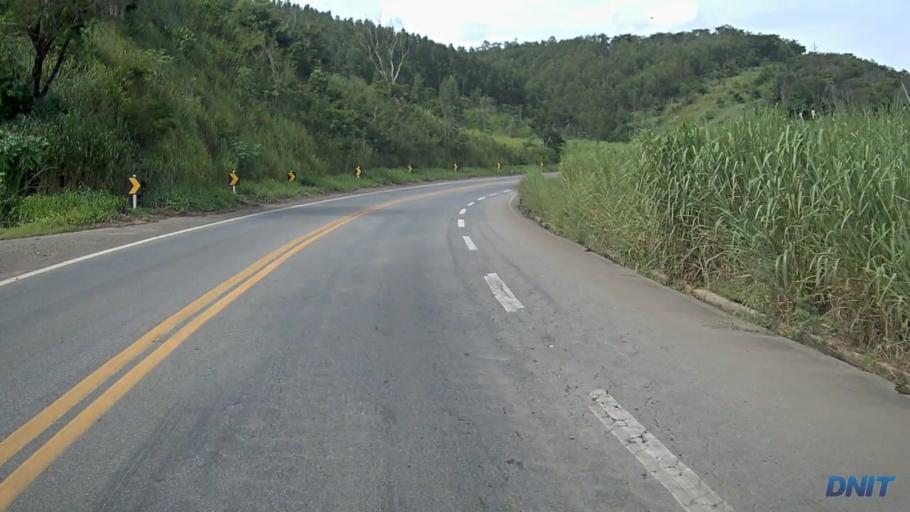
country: BR
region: Minas Gerais
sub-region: Ipaba
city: Ipaba
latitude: -19.3612
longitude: -42.4475
